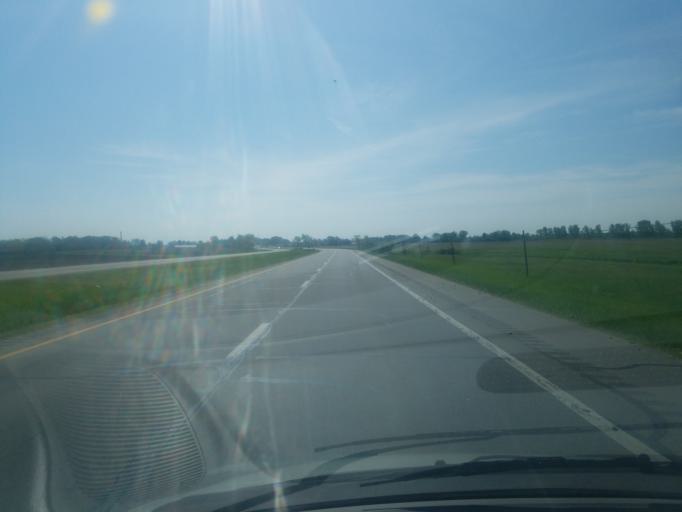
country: US
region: Ohio
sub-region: Huron County
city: Monroeville
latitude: 41.2595
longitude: -82.7632
